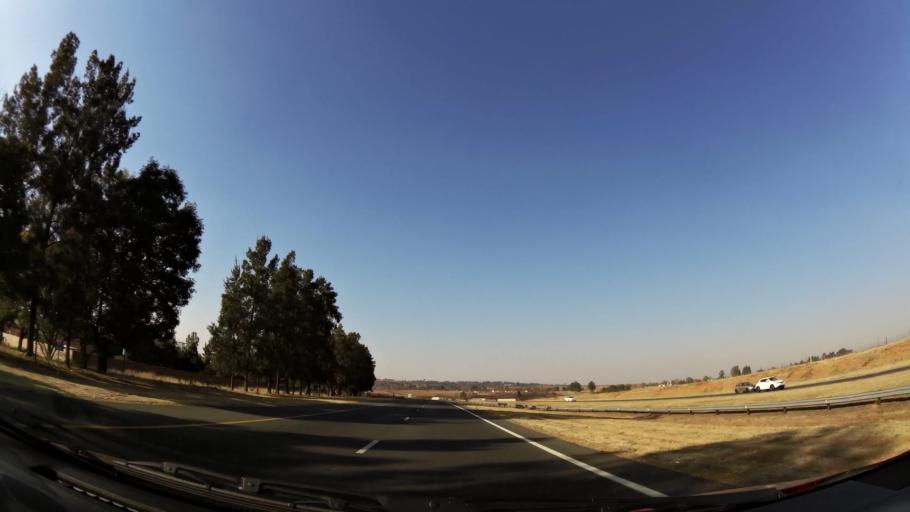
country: ZA
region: Gauteng
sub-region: West Rand District Municipality
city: Muldersdriseloop
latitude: -26.0078
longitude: 27.8920
